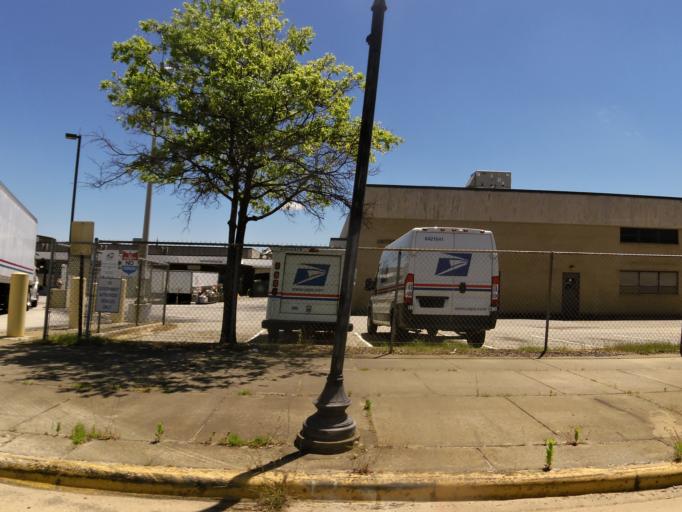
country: US
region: Georgia
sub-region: Richmond County
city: Augusta
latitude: 33.4710
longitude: -81.9700
